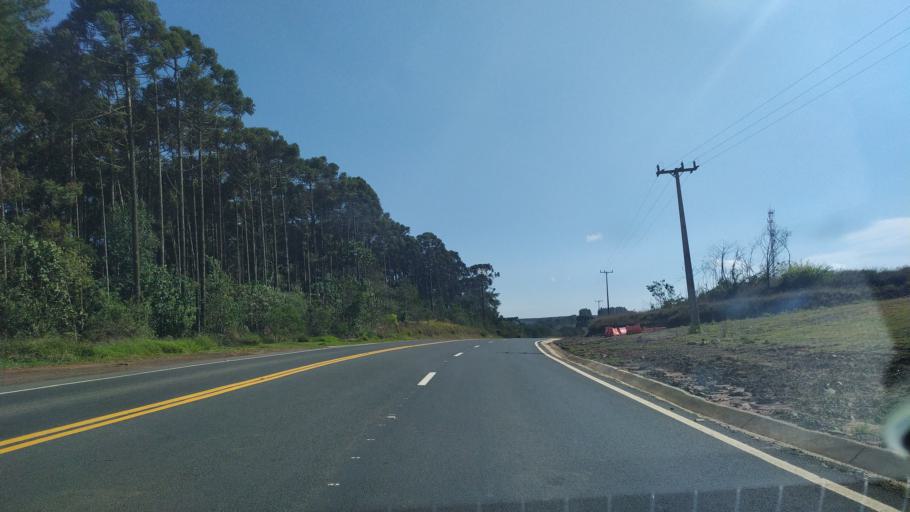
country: BR
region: Parana
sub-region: Telemaco Borba
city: Telemaco Borba
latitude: -24.2536
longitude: -50.7424
